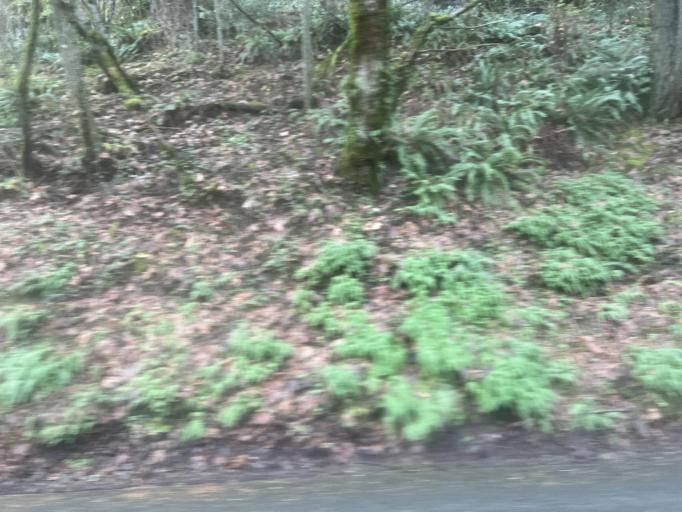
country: US
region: Washington
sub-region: Clark County
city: Washougal
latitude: 45.5419
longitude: -122.2051
